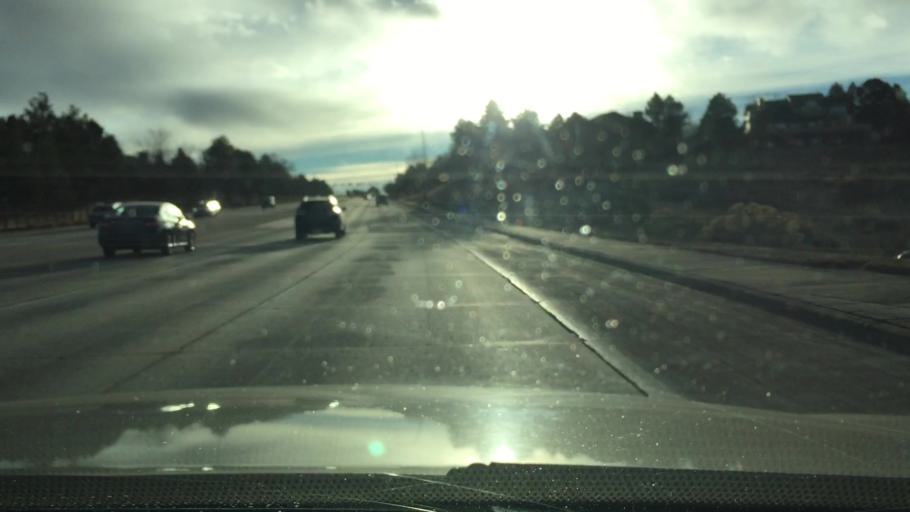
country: US
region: Colorado
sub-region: Douglas County
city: Highlands Ranch
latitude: 39.5414
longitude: -104.9664
